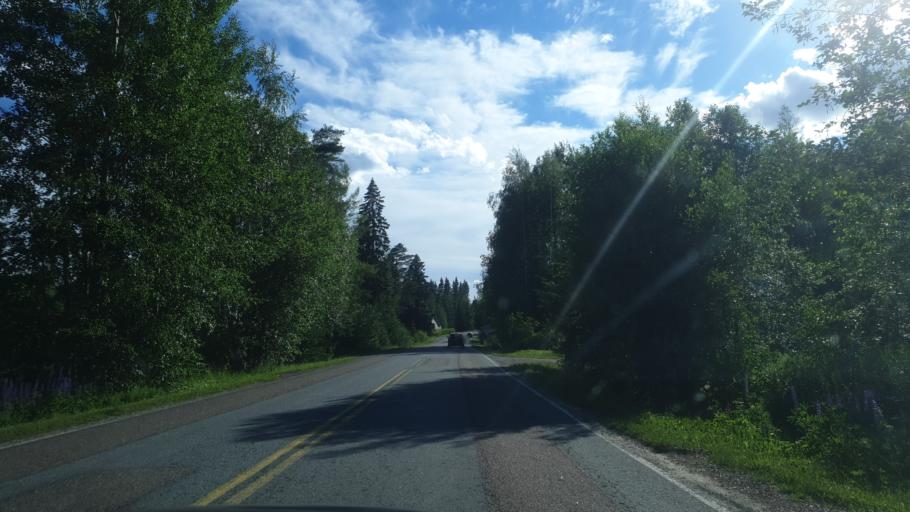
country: FI
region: Southern Savonia
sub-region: Mikkeli
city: Pertunmaa
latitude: 61.5209
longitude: 26.5003
